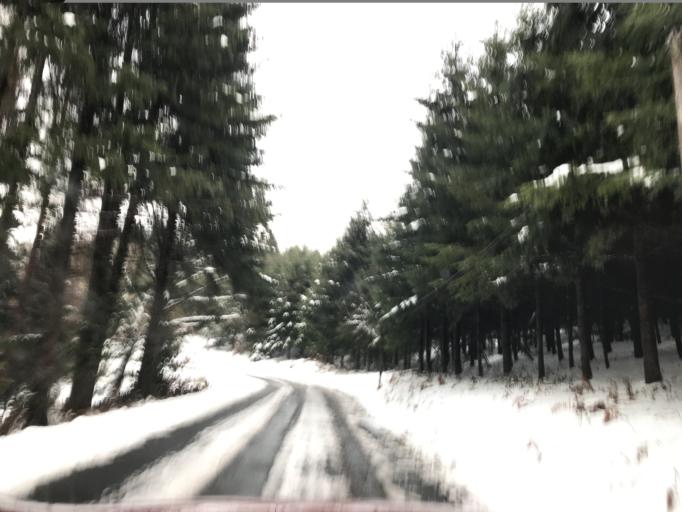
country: FR
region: Auvergne
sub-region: Departement du Puy-de-Dome
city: Celles-sur-Durolle
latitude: 45.7525
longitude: 3.6636
